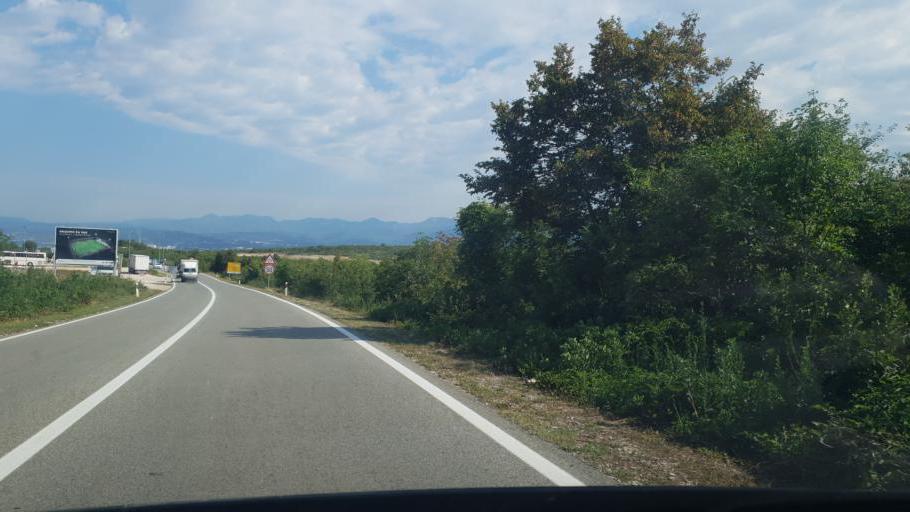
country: HR
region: Primorsko-Goranska
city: Omisalj
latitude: 45.2160
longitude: 14.5665
